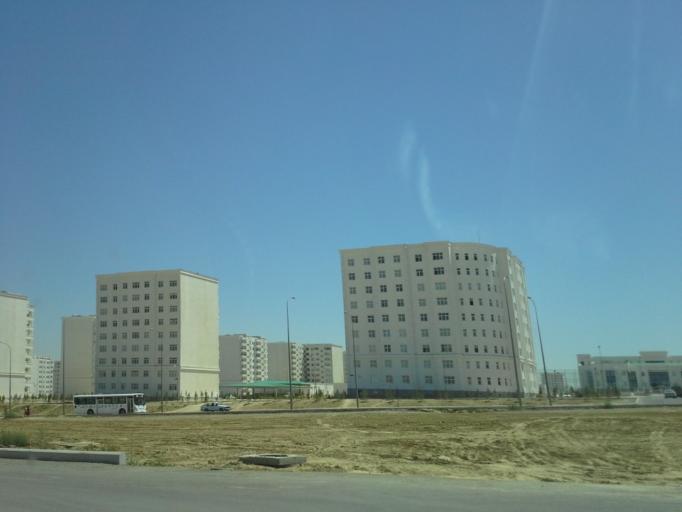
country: TM
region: Ahal
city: Ashgabat
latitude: 37.8928
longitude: 58.4047
